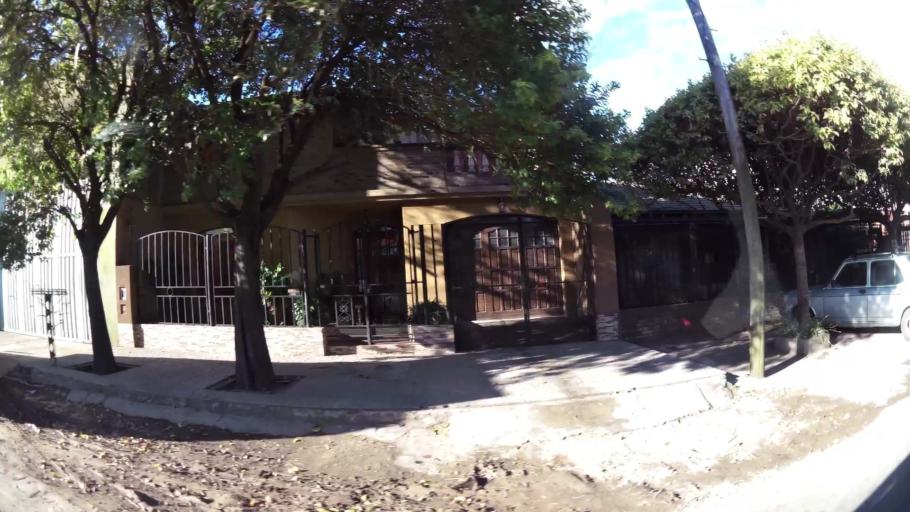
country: AR
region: Santa Fe
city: Gobernador Galvez
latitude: -32.9890
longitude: -60.6712
